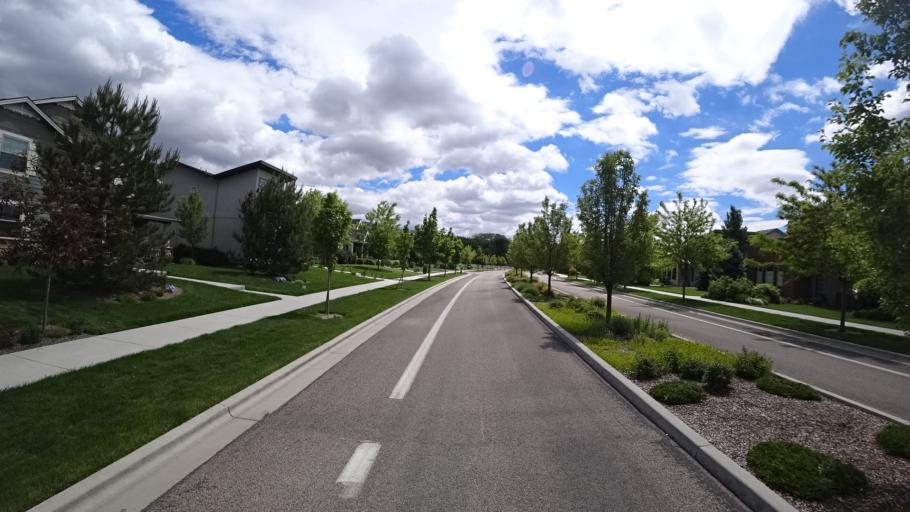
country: US
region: Idaho
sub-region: Ada County
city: Boise
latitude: 43.5779
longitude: -116.1338
